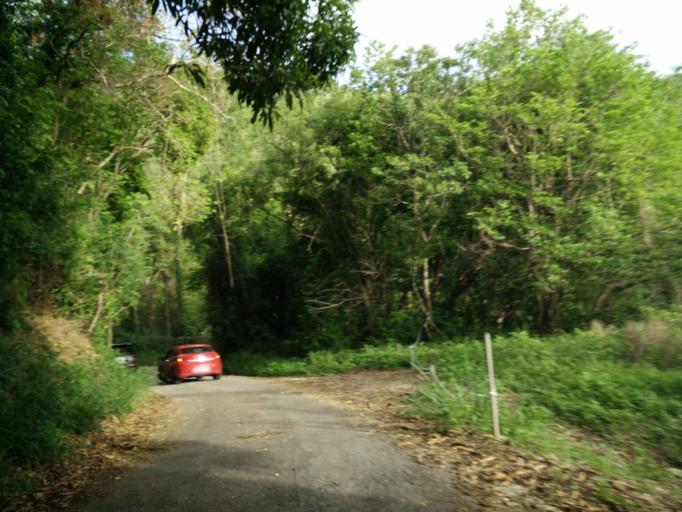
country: MQ
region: Martinique
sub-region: Martinique
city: Saint-Pierre
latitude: 14.7168
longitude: -61.1660
